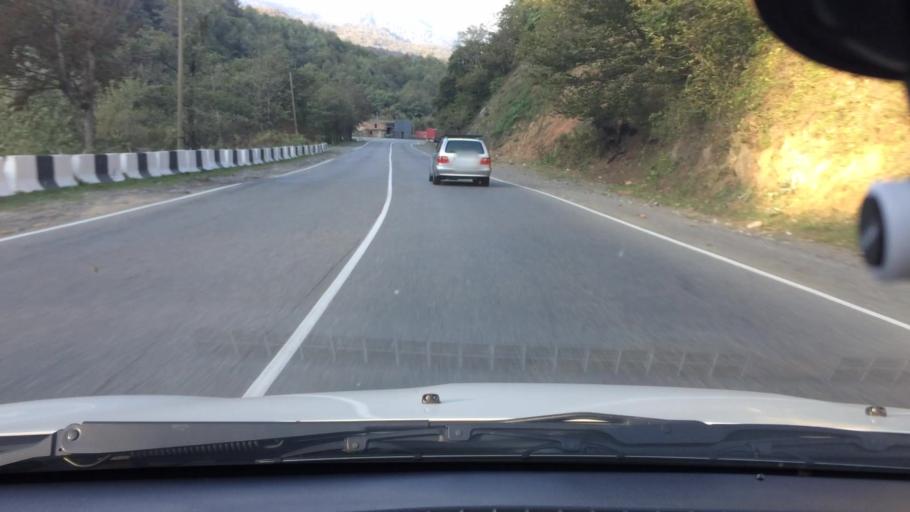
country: GE
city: Surami
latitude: 42.0967
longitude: 43.4346
